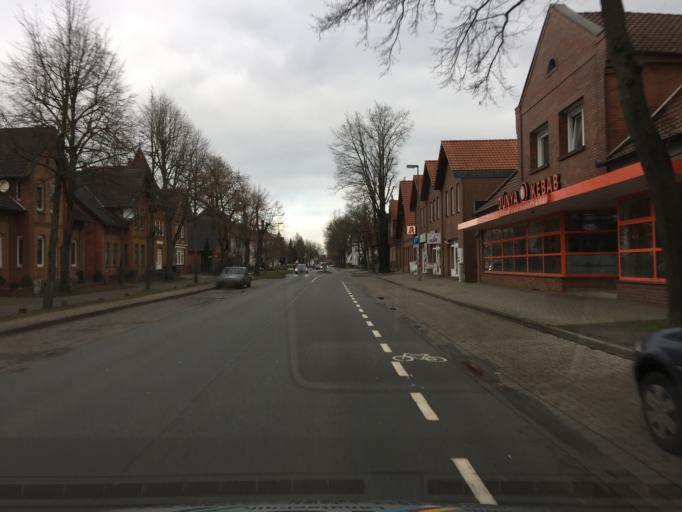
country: DE
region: Lower Saxony
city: Stolzenau
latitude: 52.5130
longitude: 9.0766
